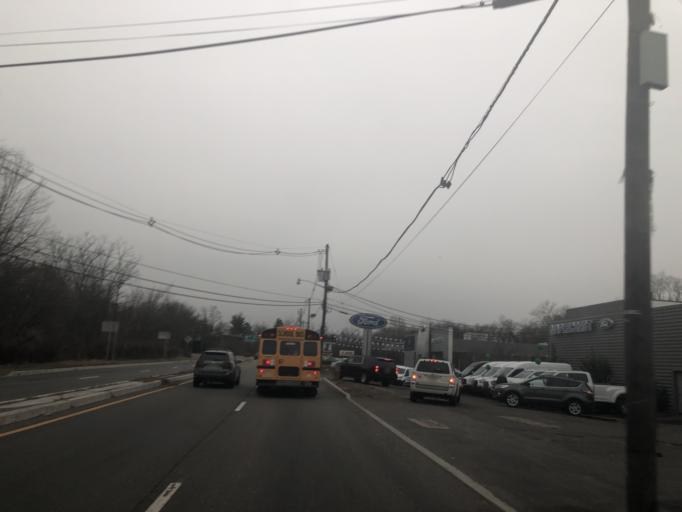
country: US
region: New Jersey
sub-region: Essex County
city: Maplewood
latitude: 40.7169
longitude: -74.2936
